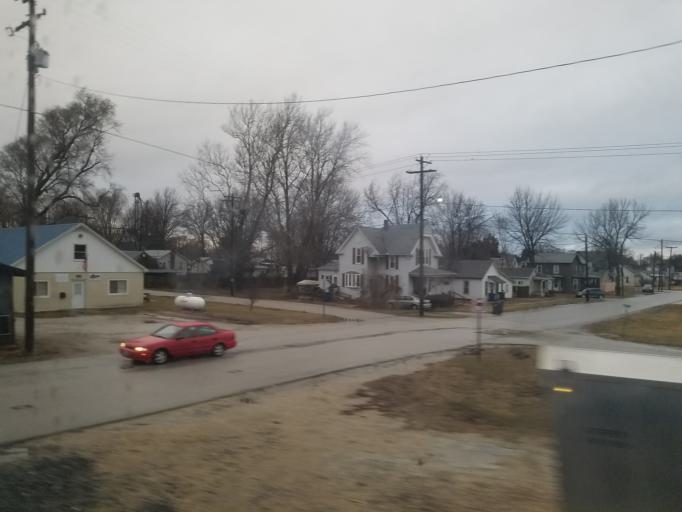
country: US
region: Illinois
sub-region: Warren County
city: Monmouth
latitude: 40.9065
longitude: -90.6533
